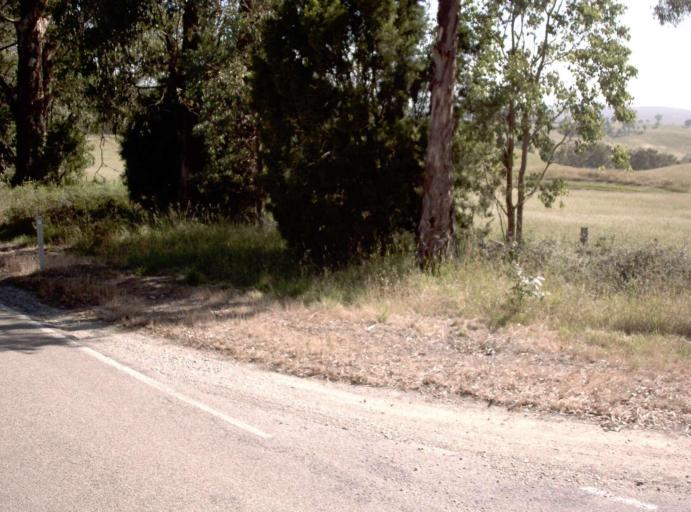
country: AU
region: Victoria
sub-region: East Gippsland
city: Lakes Entrance
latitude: -37.7641
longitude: 147.8123
